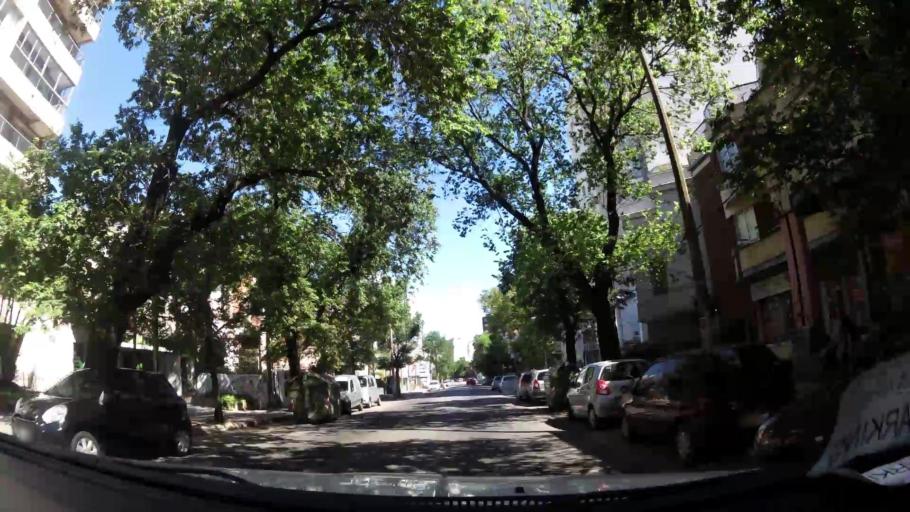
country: UY
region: Montevideo
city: Montevideo
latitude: -34.9159
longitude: -56.1590
